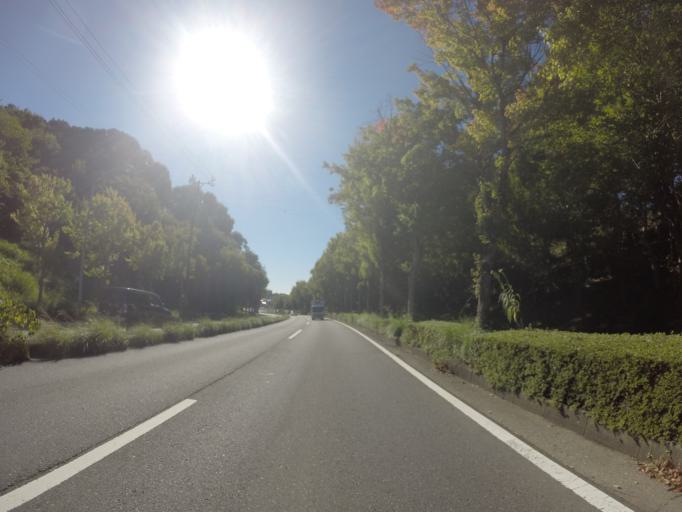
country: JP
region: Shizuoka
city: Fujieda
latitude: 34.8588
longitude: 138.2405
